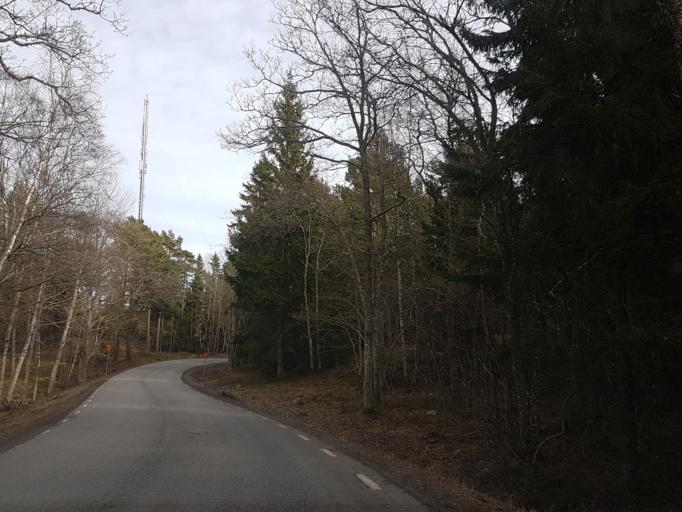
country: SE
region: Stockholm
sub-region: Norrtalje Kommun
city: Bjorko
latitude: 59.6606
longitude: 18.9077
